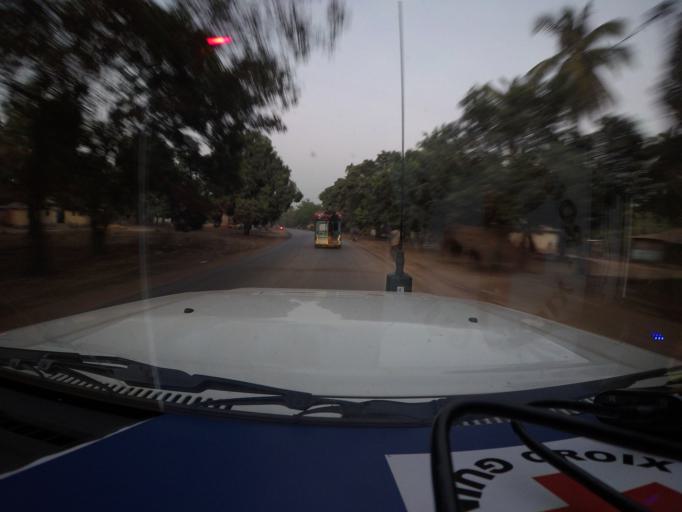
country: GN
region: Kindia
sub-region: Kindia
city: Kindia
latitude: 9.9502
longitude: -12.9496
